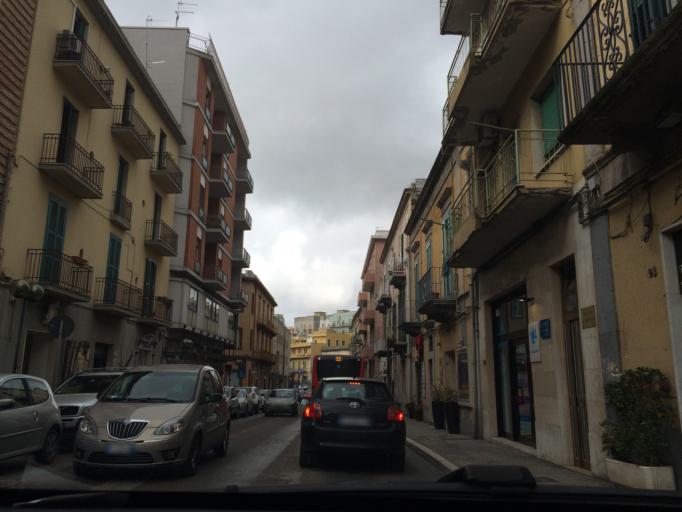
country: IT
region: Basilicate
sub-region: Provincia di Matera
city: Matera
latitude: 40.6655
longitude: 16.6058
